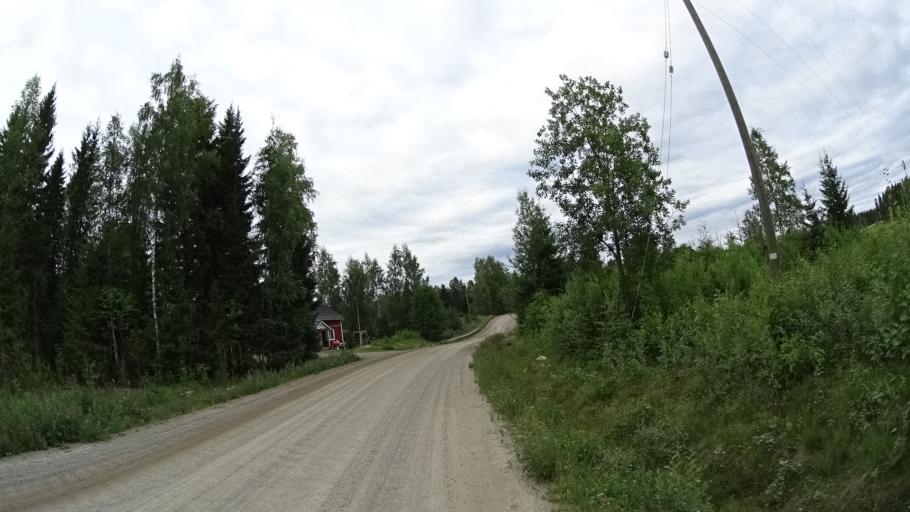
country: FI
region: Satakunta
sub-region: Pohjois-Satakunta
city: Jaemijaervi
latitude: 61.7690
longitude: 22.8460
